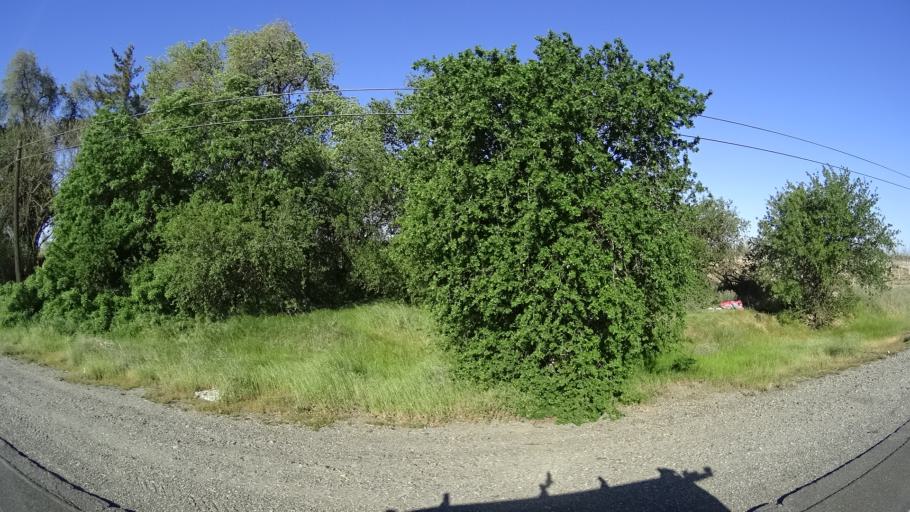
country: US
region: California
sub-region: Glenn County
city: Orland
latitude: 39.7704
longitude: -122.1968
